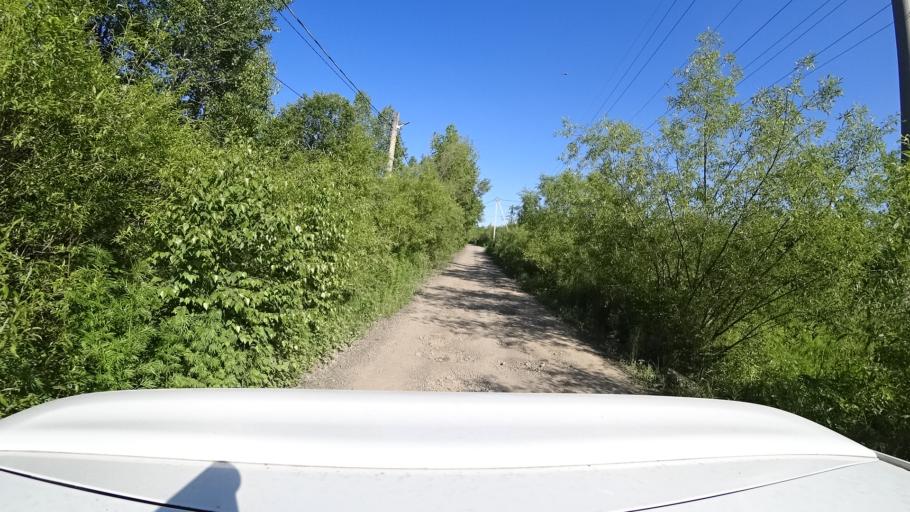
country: RU
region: Khabarovsk Krai
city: Topolevo
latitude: 48.5418
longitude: 135.1711
